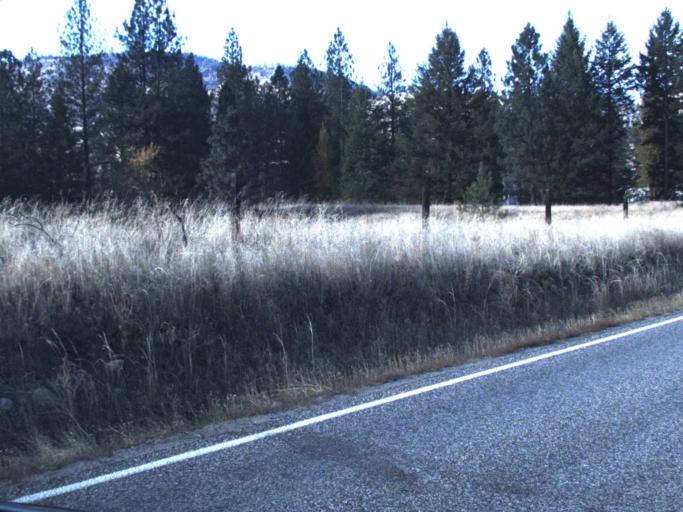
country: CA
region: British Columbia
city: Rossland
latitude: 48.8564
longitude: -117.8790
